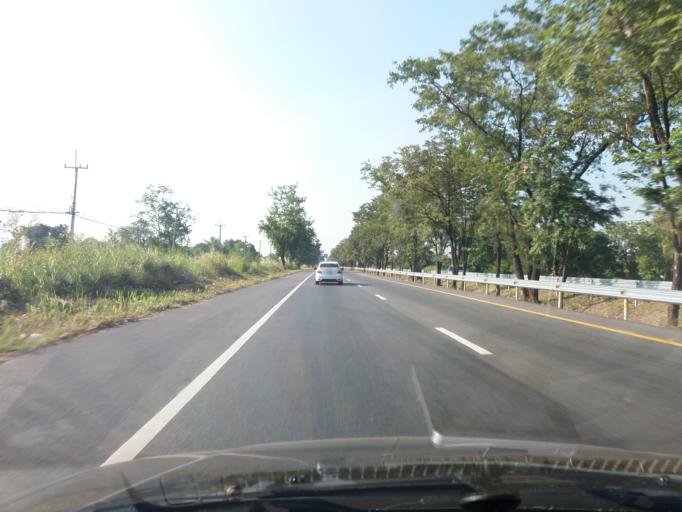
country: TH
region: Nakhon Sawan
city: Kao Liao
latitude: 15.8023
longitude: 99.9551
